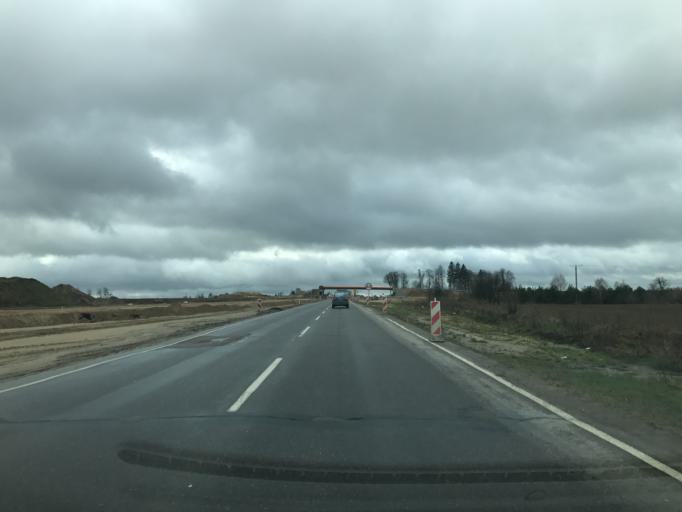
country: PL
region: Warmian-Masurian Voivodeship
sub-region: Powiat olsztynski
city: Stawiguda
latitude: 53.6274
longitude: 20.3496
